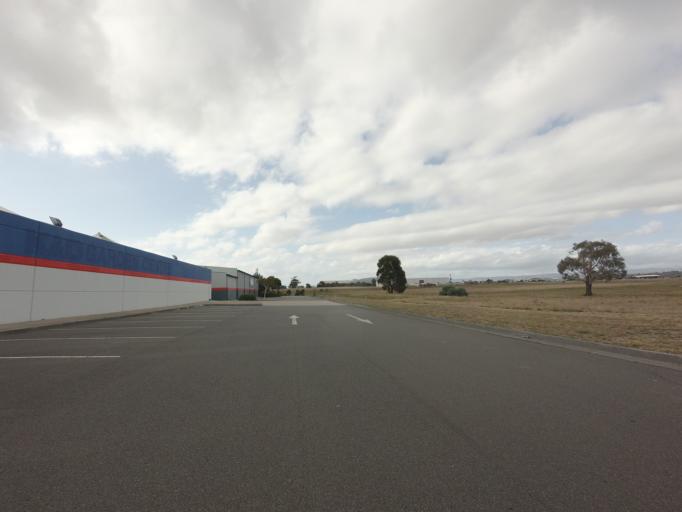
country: AU
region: Tasmania
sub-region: Clarence
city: Cambridge
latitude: -42.8341
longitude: 147.4708
